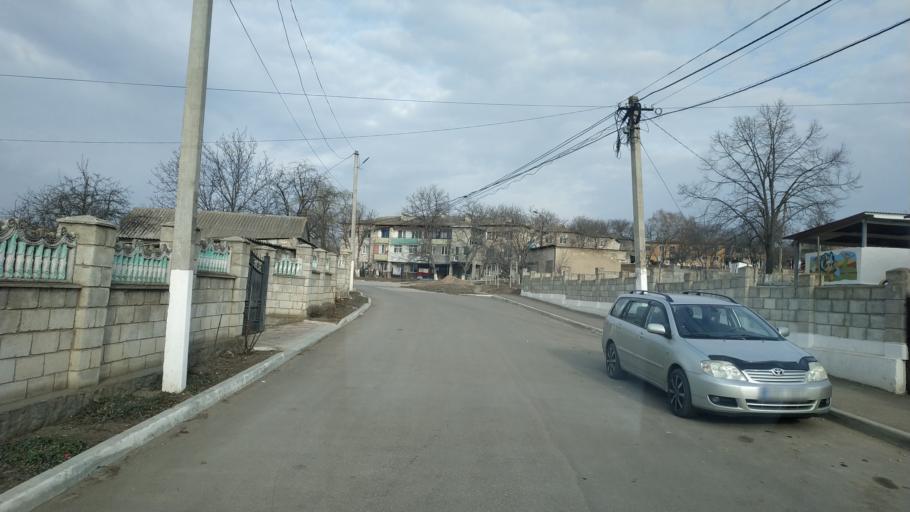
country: MD
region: Chisinau
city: Vadul lui Voda
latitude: 47.0094
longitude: 29.1220
